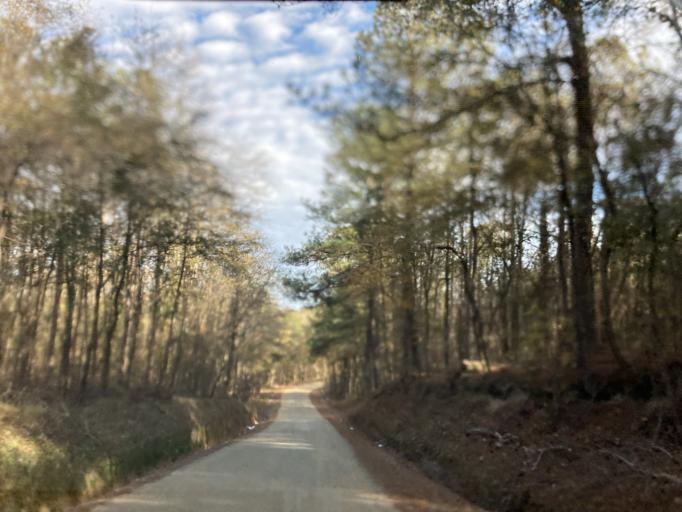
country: US
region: Georgia
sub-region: Jones County
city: Gray
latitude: 32.9111
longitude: -83.4961
